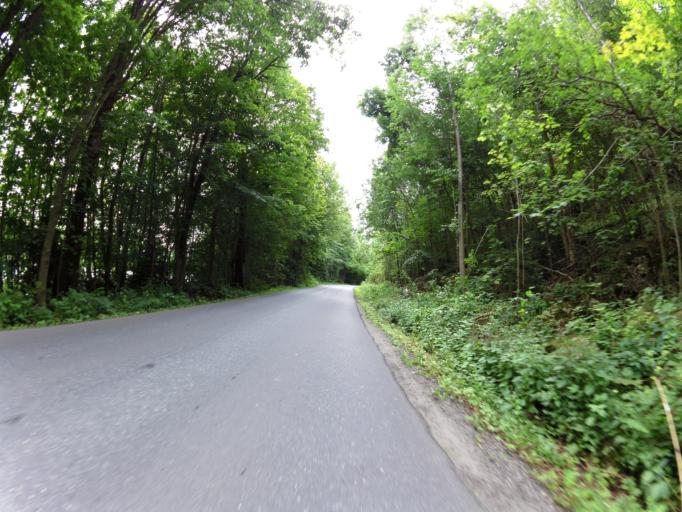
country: NO
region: Akershus
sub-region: As
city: As
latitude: 59.6978
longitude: 10.7382
